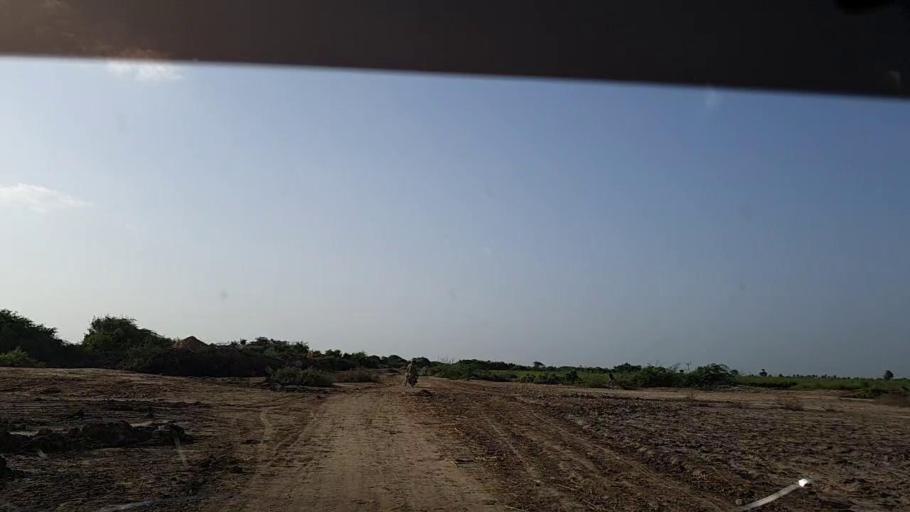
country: PK
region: Sindh
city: Badin
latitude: 24.5722
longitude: 68.8766
